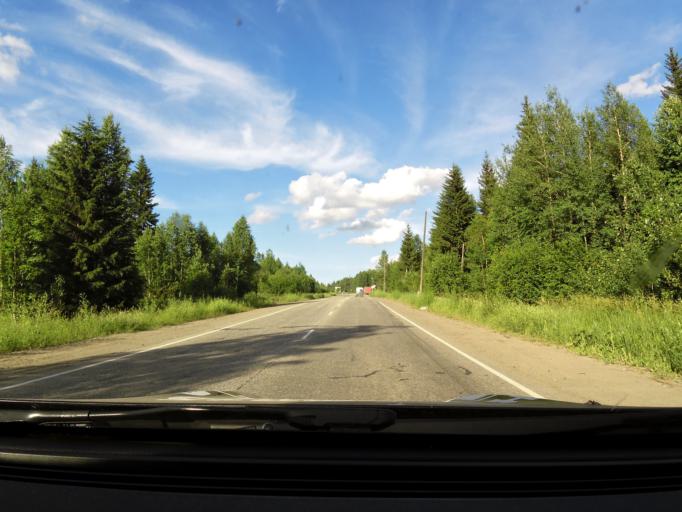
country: RU
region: Kirov
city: Omutninsk
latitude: 58.6983
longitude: 52.2292
